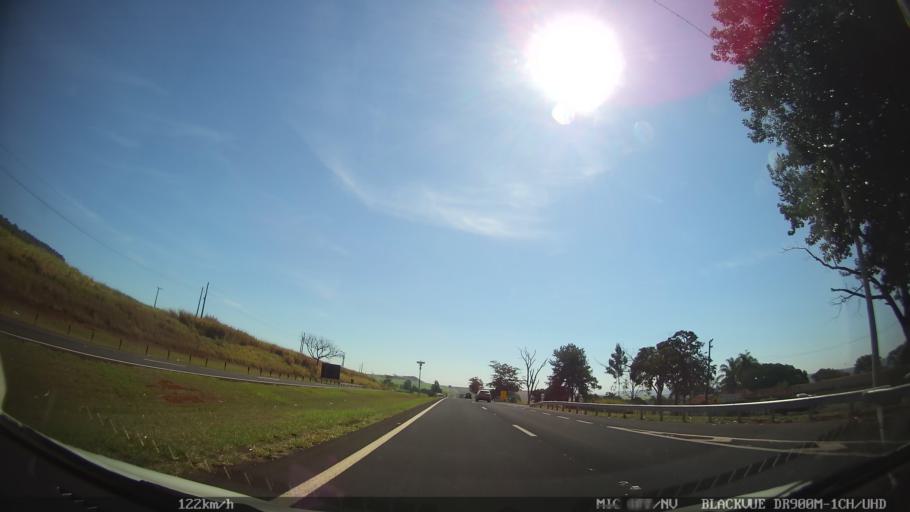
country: BR
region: Sao Paulo
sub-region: Sao Simao
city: Sao Simao
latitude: -21.4628
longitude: -47.6428
